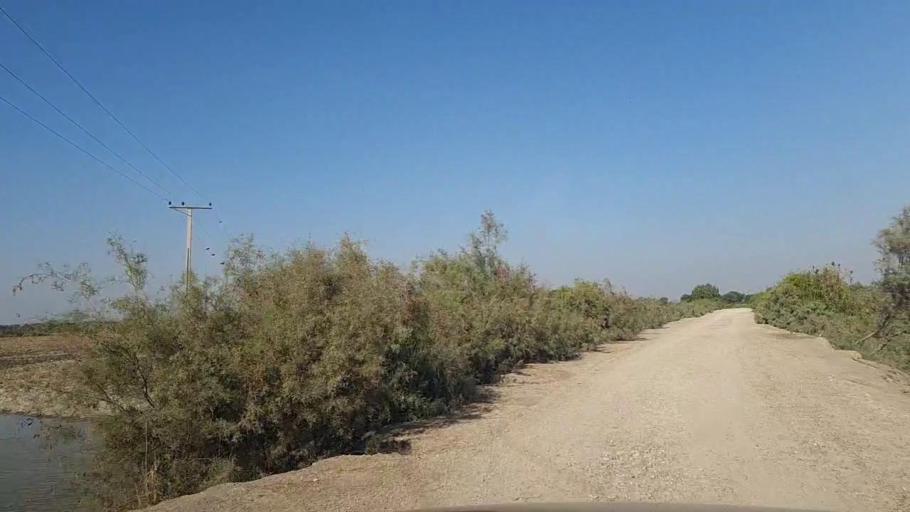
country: PK
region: Sindh
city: Mirpur Batoro
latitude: 24.7432
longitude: 68.3407
